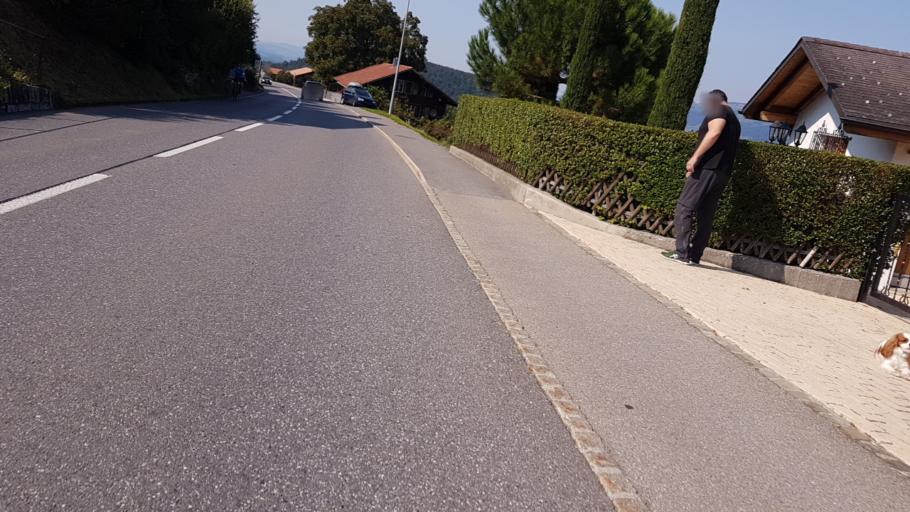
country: CH
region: Bern
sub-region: Frutigen-Niedersimmental District
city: Aeschi
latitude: 46.6616
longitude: 7.6927
